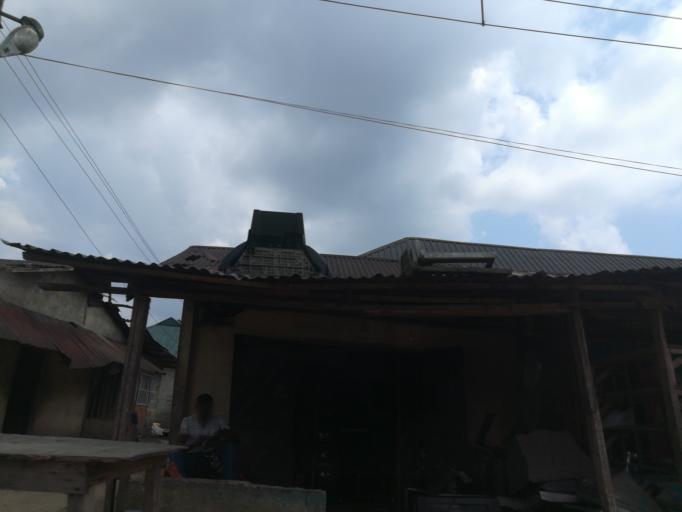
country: NG
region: Rivers
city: Okrika
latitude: 4.7269
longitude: 7.1509
